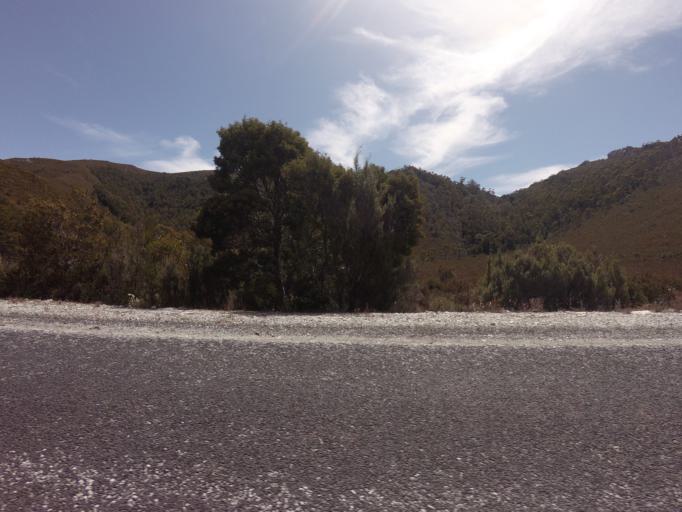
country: AU
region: Tasmania
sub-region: West Coast
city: Queenstown
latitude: -42.7948
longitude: 146.0837
